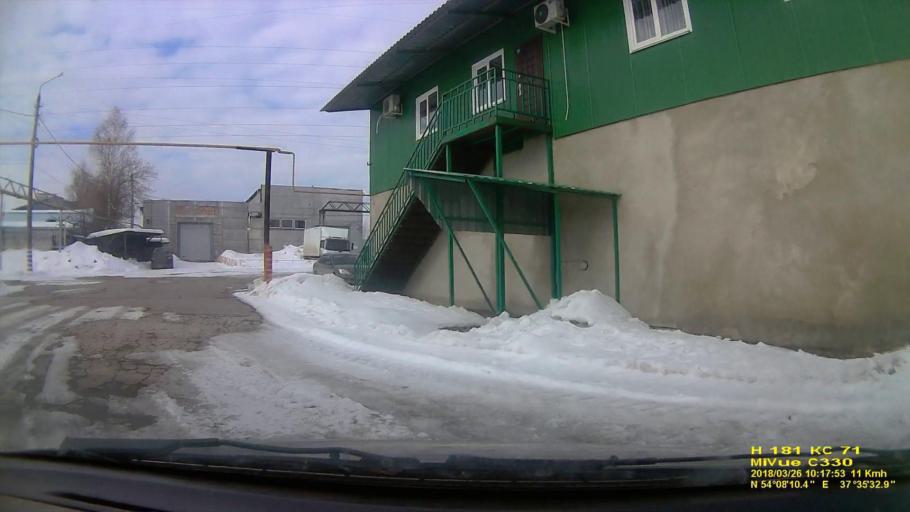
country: RU
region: Tula
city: Mendeleyevskiy
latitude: 54.1354
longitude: 37.5973
